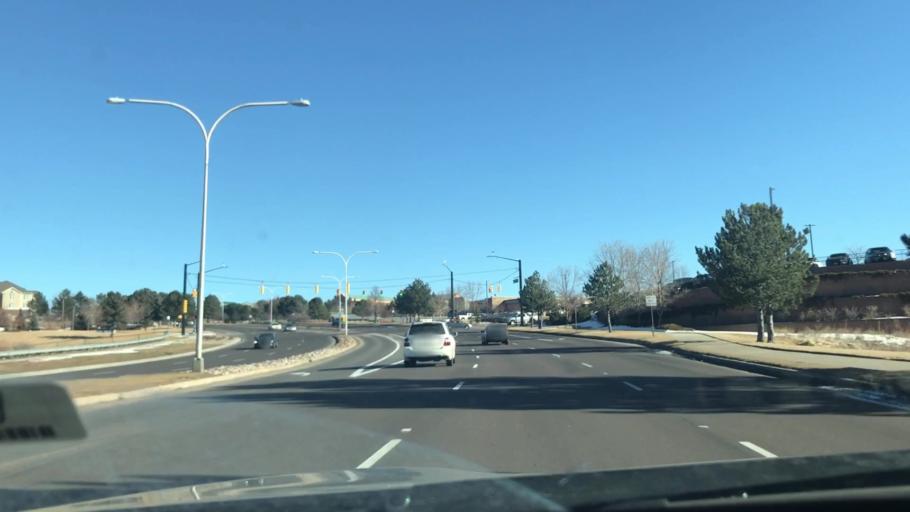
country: US
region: Colorado
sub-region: El Paso County
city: Air Force Academy
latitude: 38.9652
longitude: -104.7966
